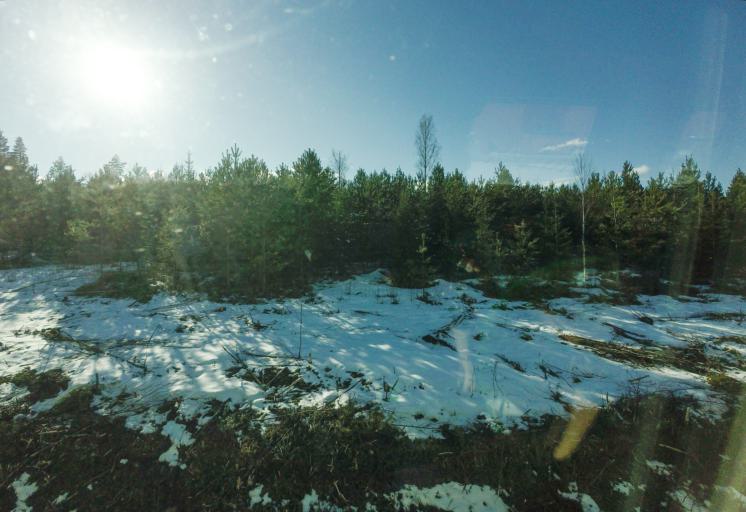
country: FI
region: South Karelia
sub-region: Imatra
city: Parikkala
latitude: 61.5384
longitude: 29.5196
